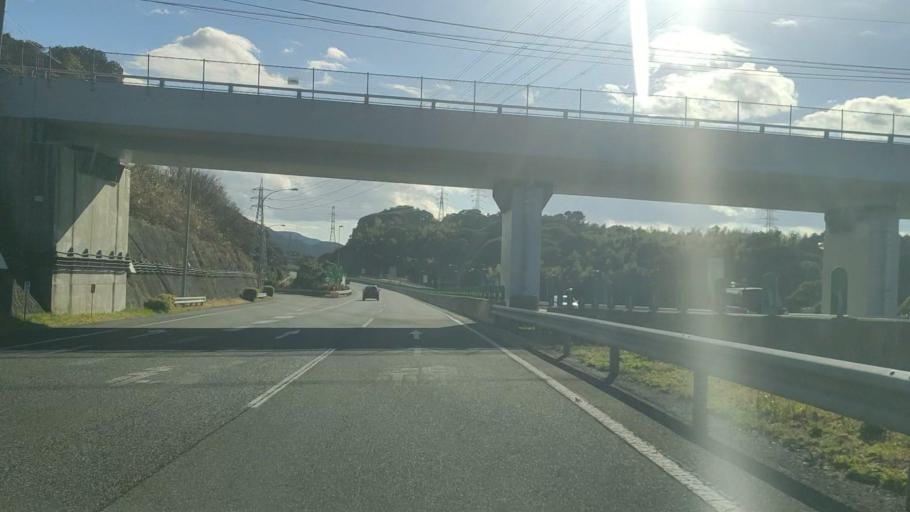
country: JP
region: Fukuoka
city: Kitakyushu
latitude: 33.8428
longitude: 130.7657
